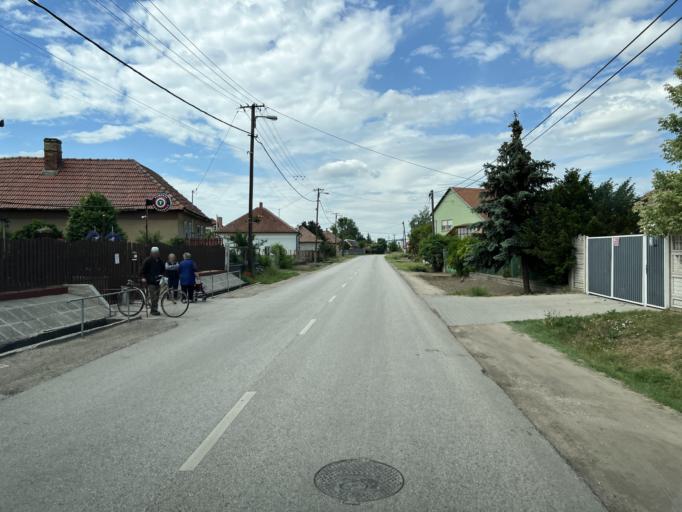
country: HU
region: Pest
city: Szentlorinckata
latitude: 47.5167
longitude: 19.7501
